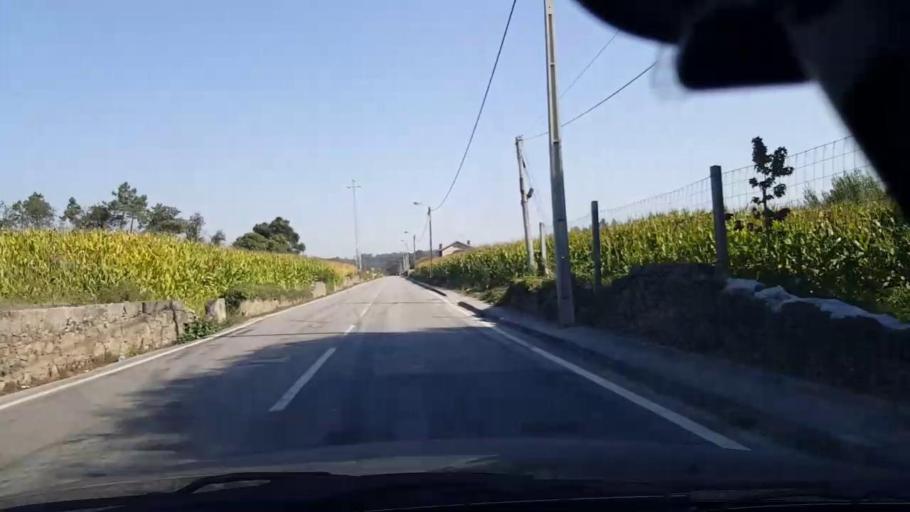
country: PT
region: Porto
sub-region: Vila do Conde
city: Arvore
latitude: 41.3431
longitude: -8.6804
